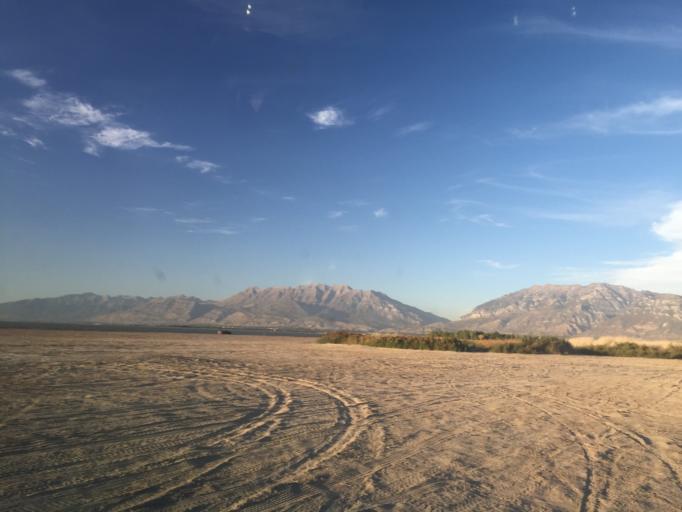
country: US
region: Utah
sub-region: Utah County
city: Benjamin
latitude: 40.1693
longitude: -111.7437
